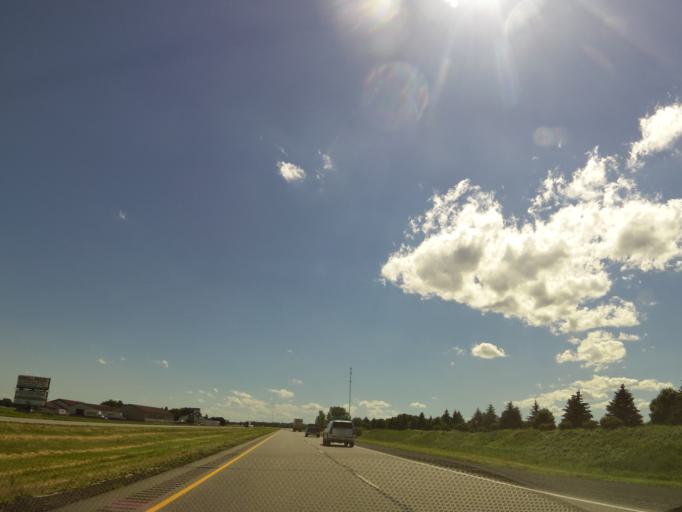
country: US
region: Minnesota
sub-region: Stearns County
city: Waite Park
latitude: 45.5337
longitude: -94.2146
